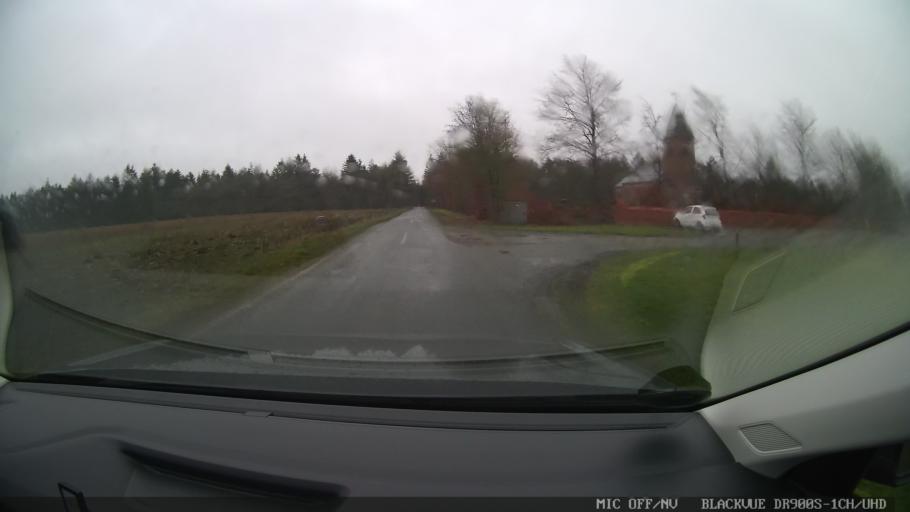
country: DK
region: Central Jutland
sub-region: Viborg Kommune
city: Karup
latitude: 56.2344
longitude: 9.1065
